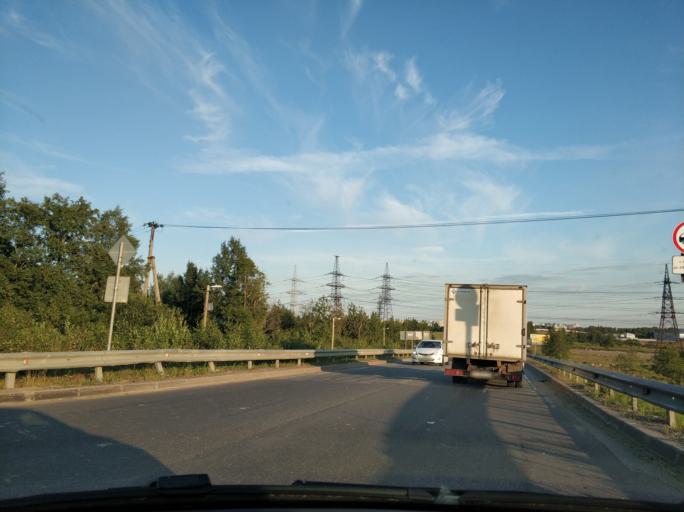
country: RU
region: Leningrad
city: Bugry
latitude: 60.1011
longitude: 30.3873
